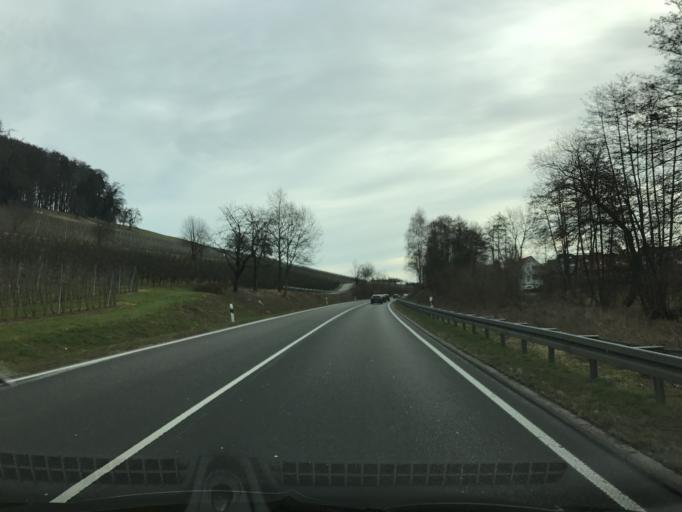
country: DE
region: Baden-Wuerttemberg
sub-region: Tuebingen Region
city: Kressbronn am Bodensee
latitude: 47.6048
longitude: 9.6125
